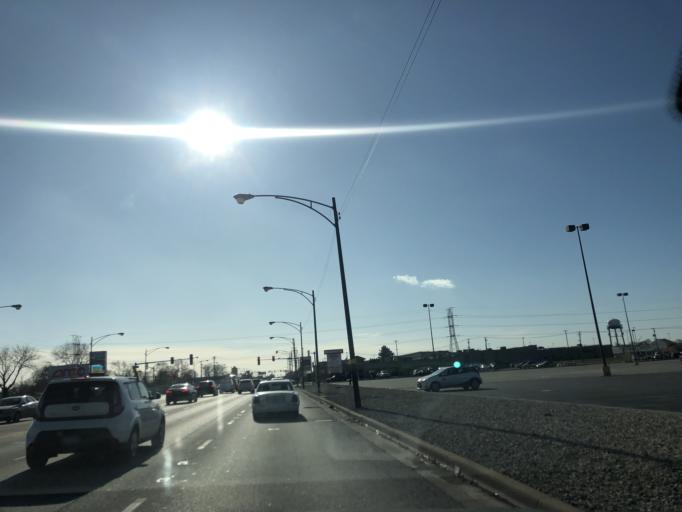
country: US
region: Illinois
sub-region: Cook County
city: Hometown
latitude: 41.7556
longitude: -87.7417
